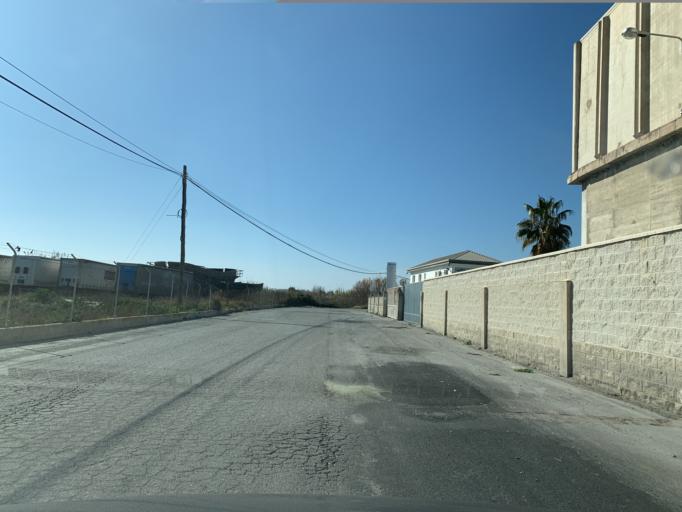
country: ES
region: Andalusia
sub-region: Provincia de Granada
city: El Varadero
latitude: 36.7268
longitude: -3.5433
